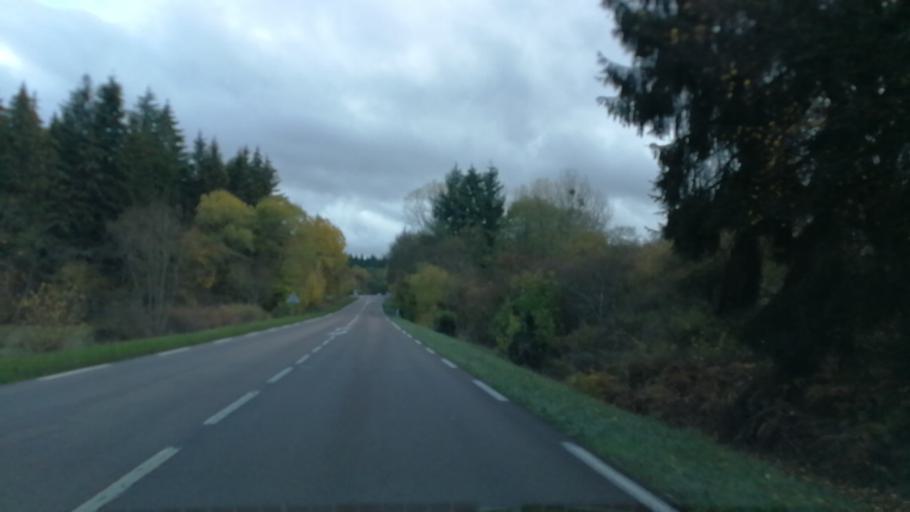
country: FR
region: Bourgogne
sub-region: Departement de la Cote-d'Or
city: Saulieu
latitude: 47.2561
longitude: 4.2708
